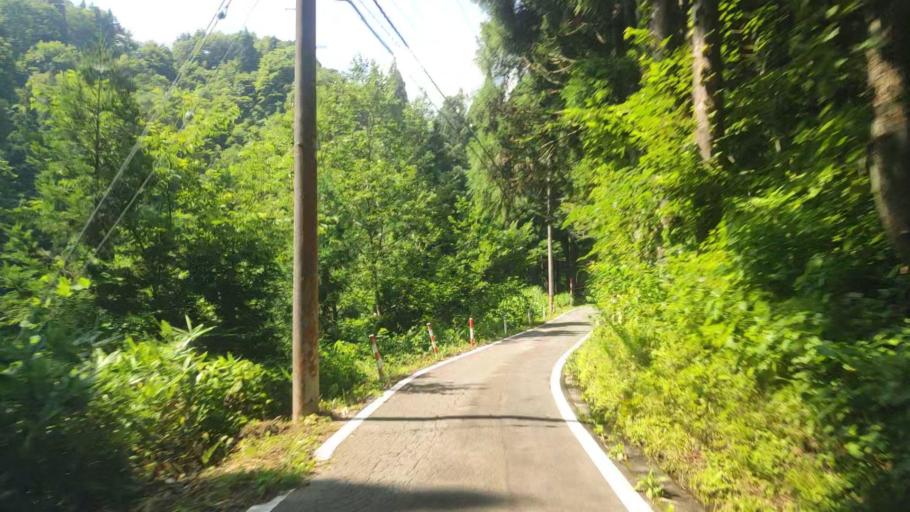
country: JP
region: Ishikawa
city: Komatsu
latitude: 36.2455
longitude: 136.5357
